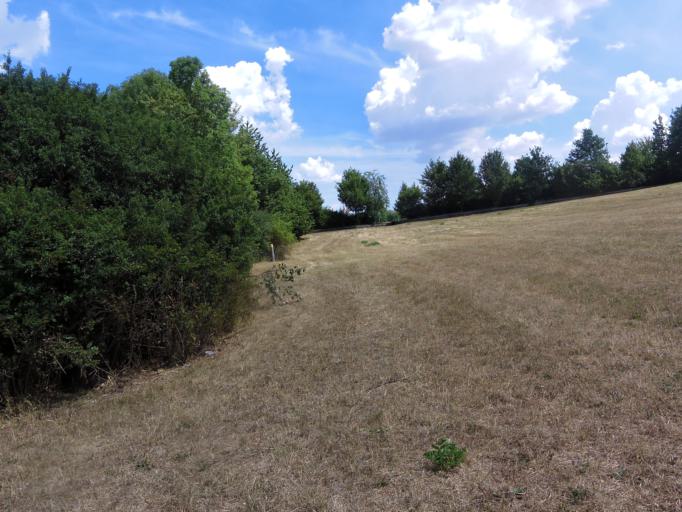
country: DE
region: Bavaria
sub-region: Regierungsbezirk Unterfranken
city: Randersacker
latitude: 49.7404
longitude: 9.9553
